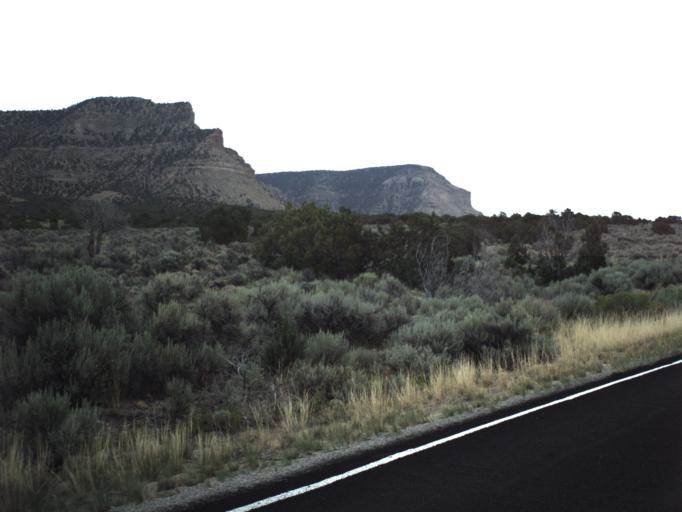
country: US
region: Utah
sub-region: Carbon County
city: East Carbon City
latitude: 39.4694
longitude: -110.3965
